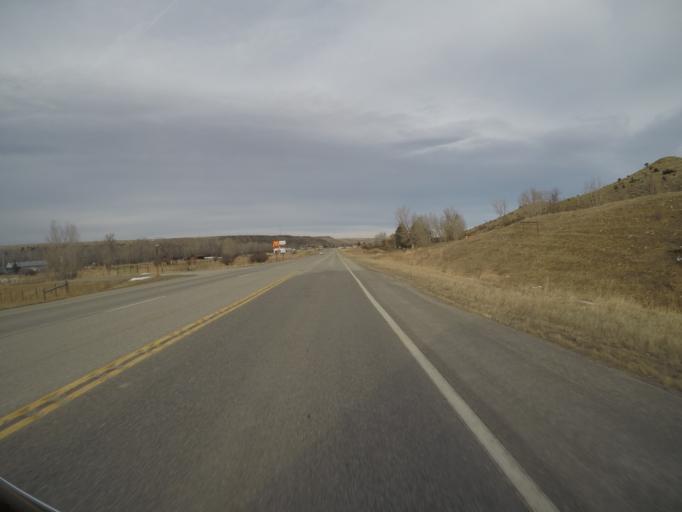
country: US
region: Montana
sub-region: Stillwater County
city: Absarokee
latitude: 45.5034
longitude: -109.4487
